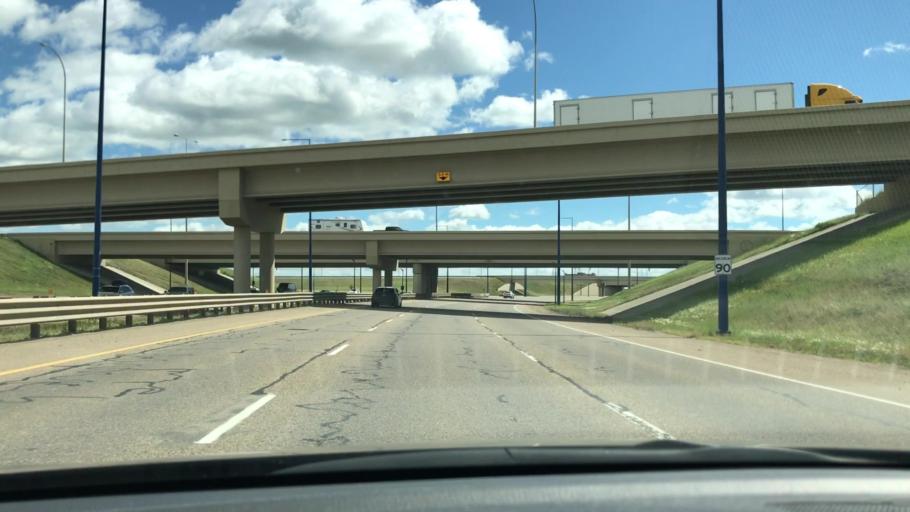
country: CA
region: Alberta
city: Edmonton
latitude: 53.4386
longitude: -113.4911
